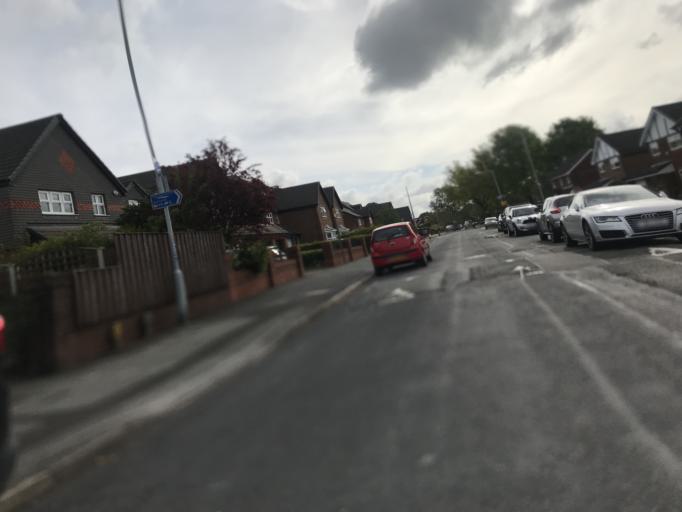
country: GB
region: England
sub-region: Manchester
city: Heaton Chapel
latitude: 53.4167
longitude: -2.1842
